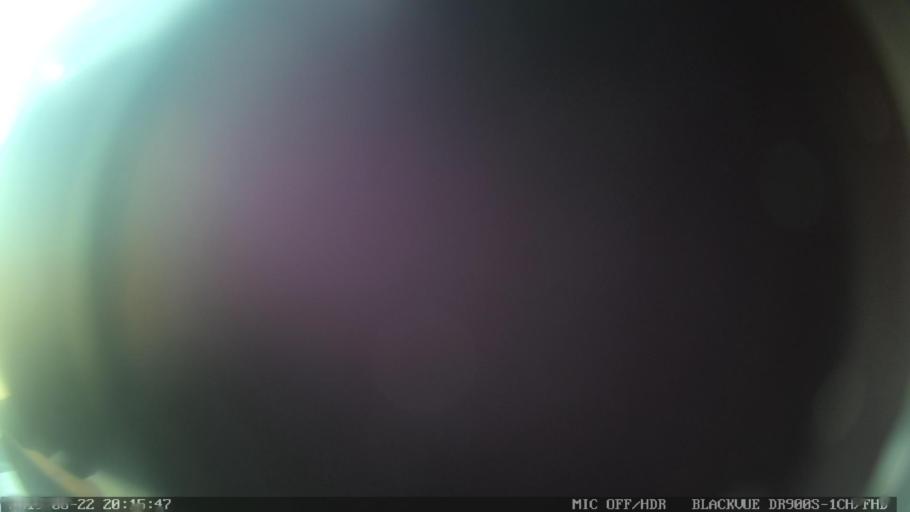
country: PT
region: Guarda
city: Alcains
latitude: 39.9232
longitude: -7.4451
